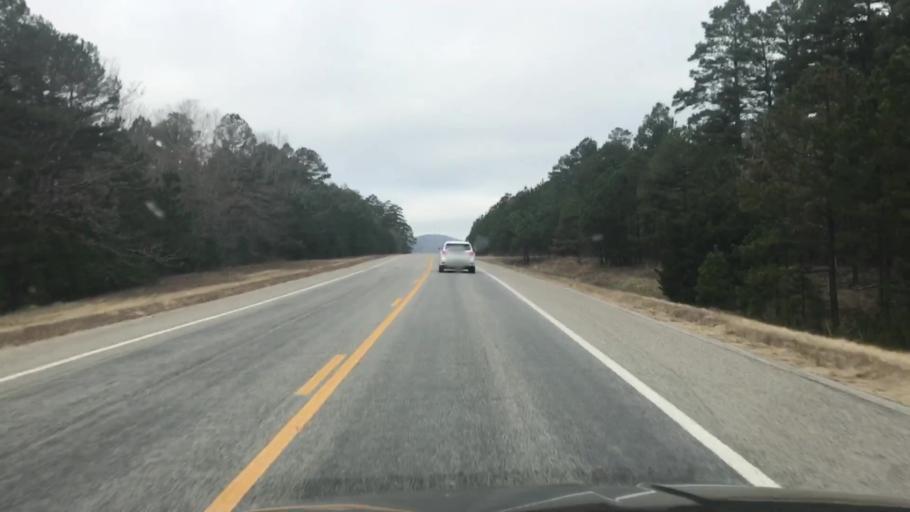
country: US
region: Arkansas
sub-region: Montgomery County
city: Mount Ida
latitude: 34.6874
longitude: -93.8798
